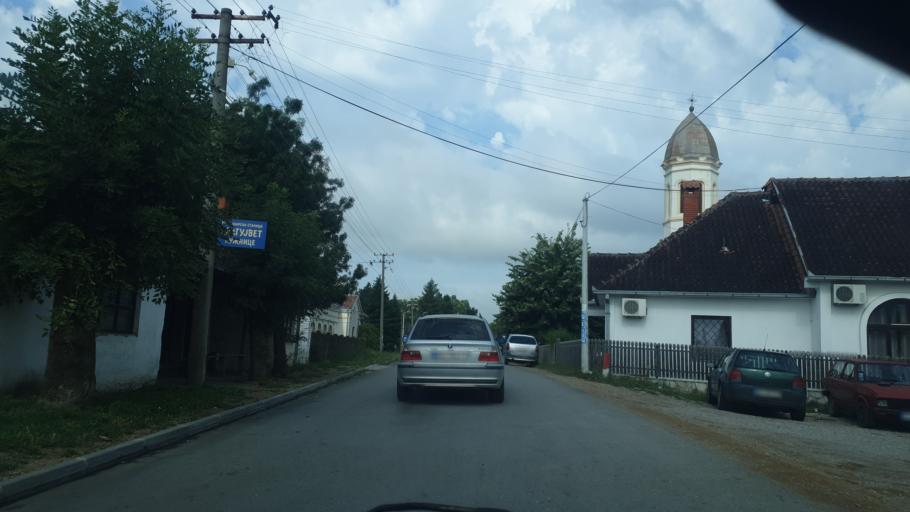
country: RS
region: Central Serbia
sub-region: Sumadijski Okrug
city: Kragujevac
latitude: 44.1073
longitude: 20.8166
